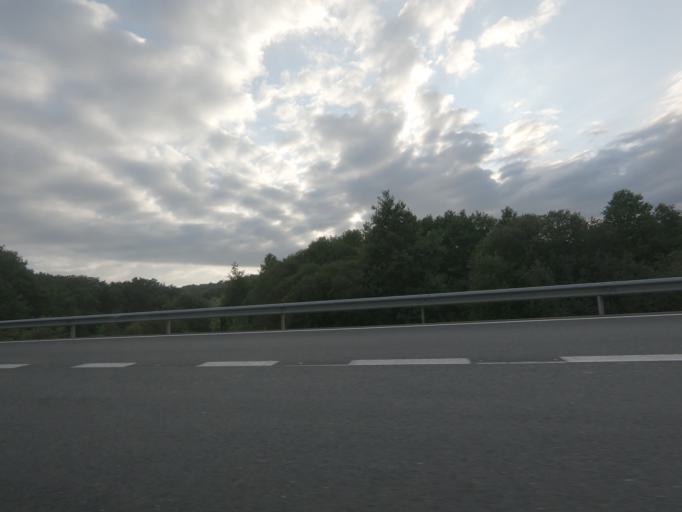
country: ES
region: Galicia
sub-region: Provincia de Ourense
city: Taboadela
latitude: 42.2463
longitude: -7.8421
